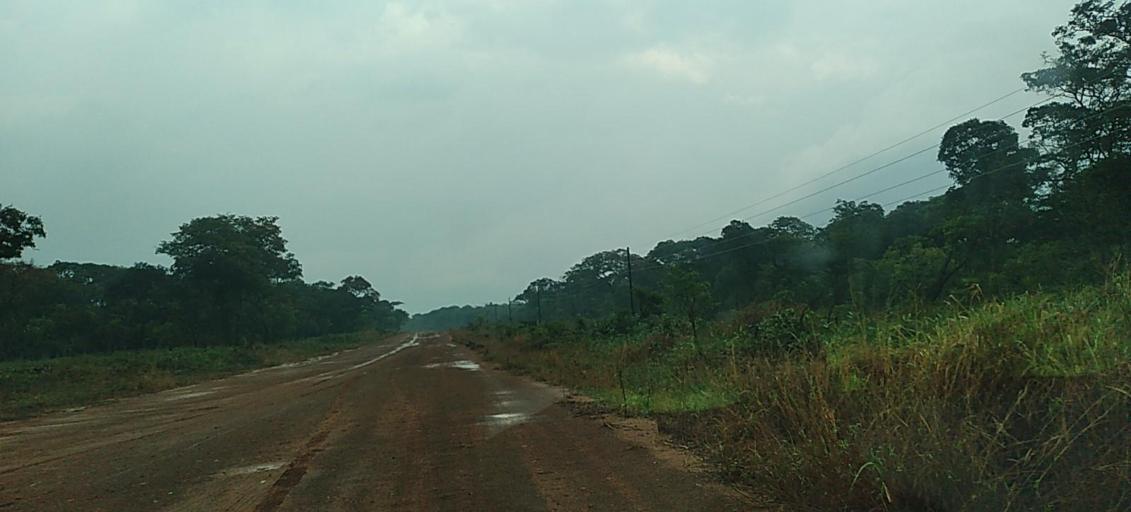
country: ZM
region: North-Western
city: Mwinilunga
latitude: -11.5827
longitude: 24.3892
